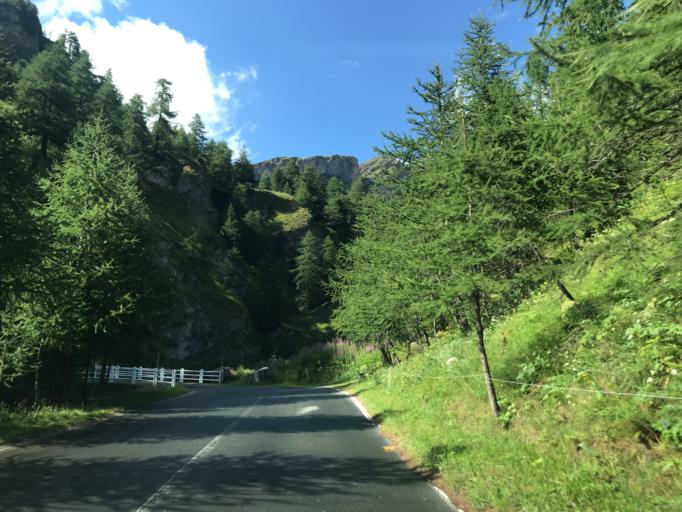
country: IT
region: Piedmont
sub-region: Provincia di Cuneo
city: Pontechianale
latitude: 44.6545
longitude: 6.9910
